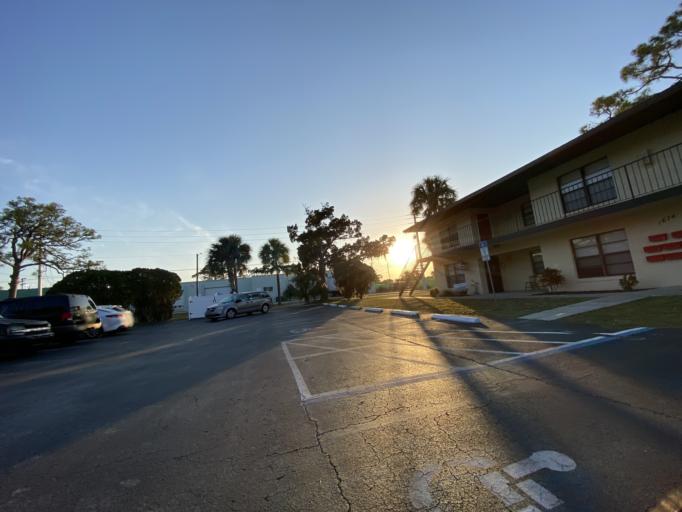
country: US
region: Florida
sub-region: Volusia County
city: South Daytona
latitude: 29.1809
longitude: -81.0094
